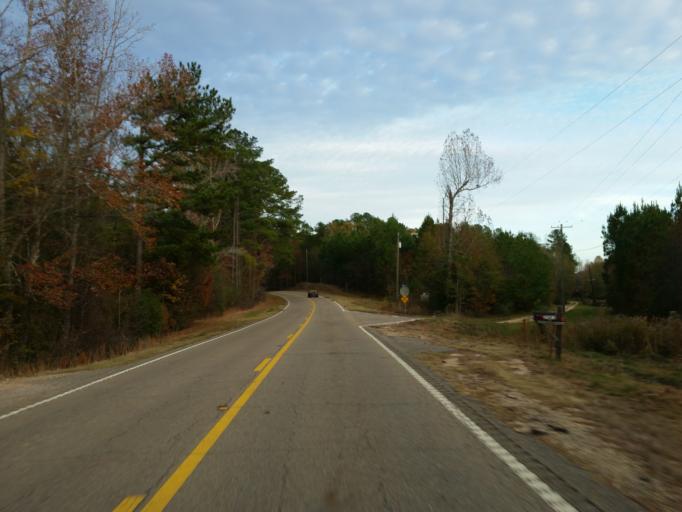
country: US
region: Mississippi
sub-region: Lauderdale County
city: Marion
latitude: 32.4125
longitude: -88.5462
